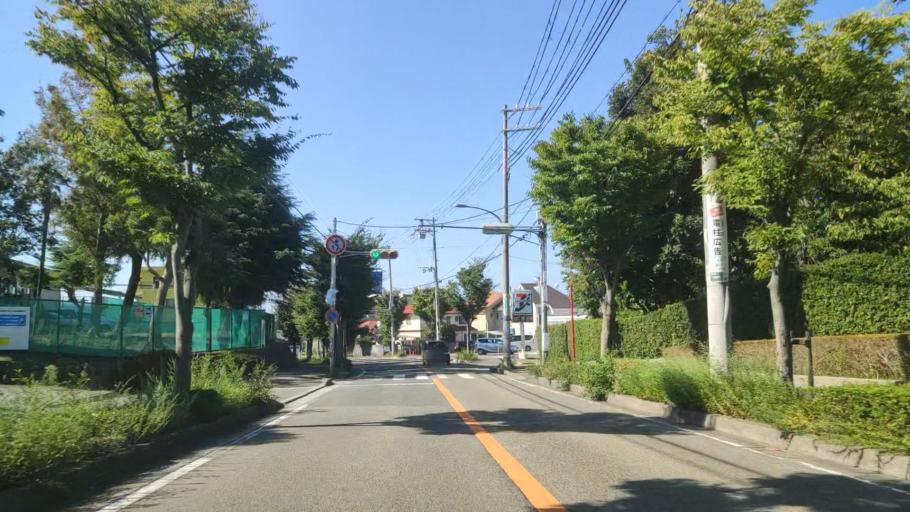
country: JP
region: Hyogo
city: Akashi
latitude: 34.6569
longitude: 135.0086
